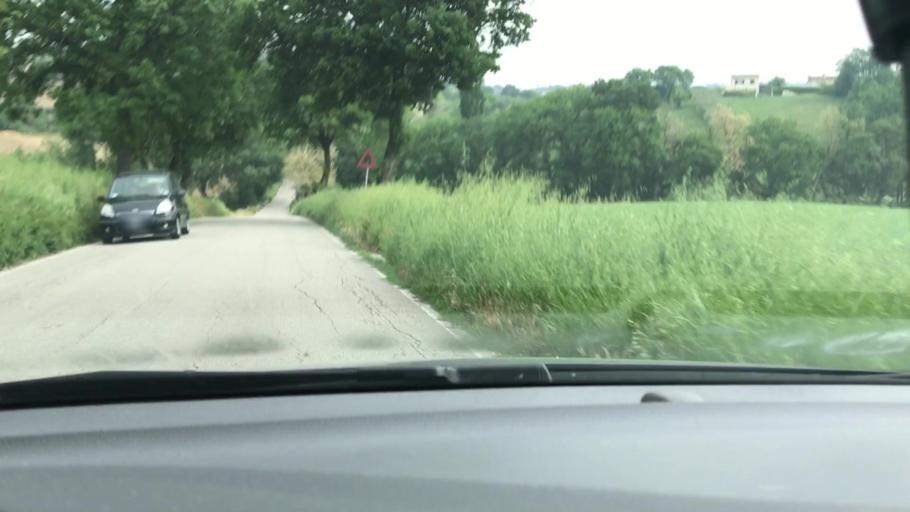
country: IT
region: The Marches
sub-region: Provincia di Macerata
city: Macerata
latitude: 43.2717
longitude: 13.4503
